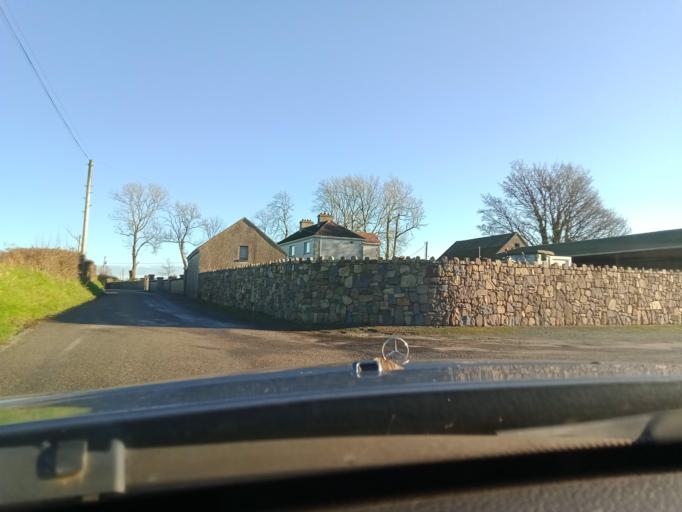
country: IE
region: Leinster
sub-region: Kilkenny
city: Mooncoin
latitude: 52.3017
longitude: -7.1949
